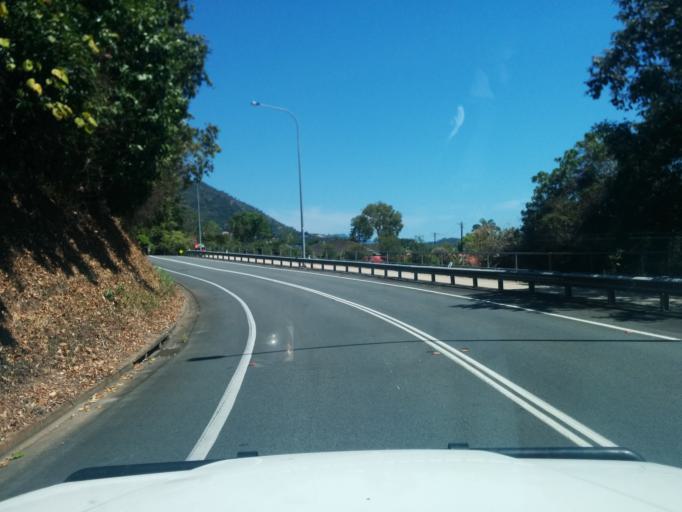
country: AU
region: Queensland
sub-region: Cairns
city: Woree
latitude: -16.9537
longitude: 145.7373
